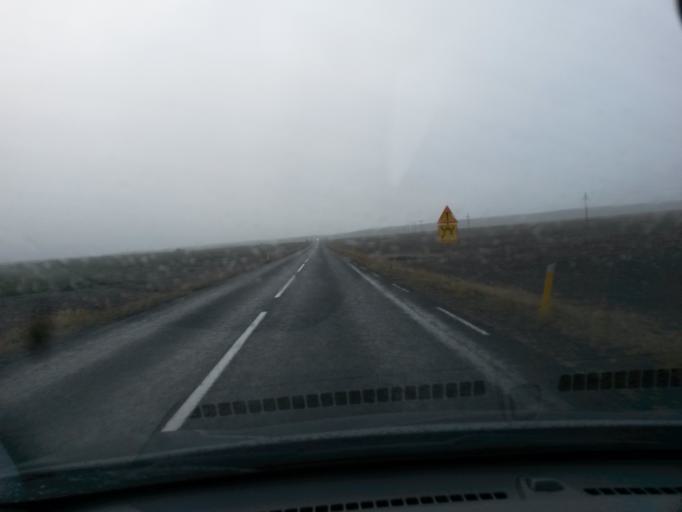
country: IS
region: South
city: Vestmannaeyjar
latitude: 63.4964
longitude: -19.3895
